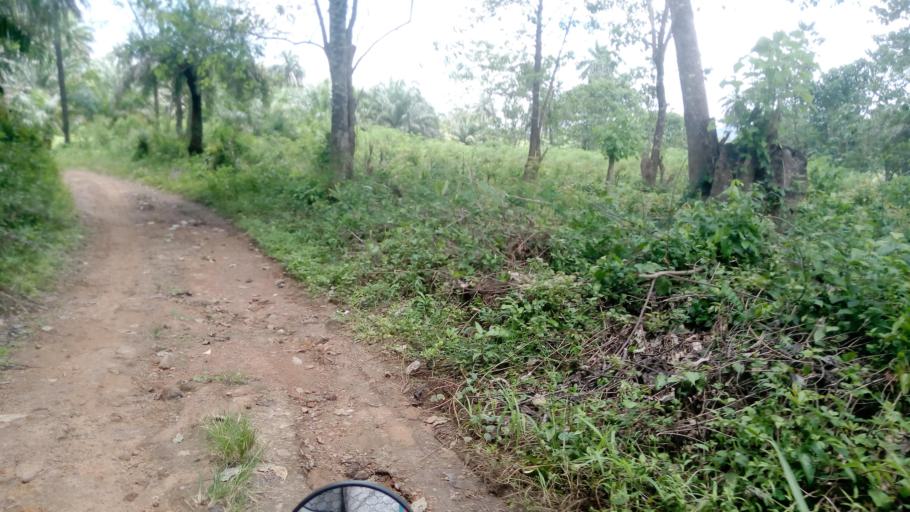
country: SL
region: Northern Province
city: Binkolo
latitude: 8.9269
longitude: -12.0091
